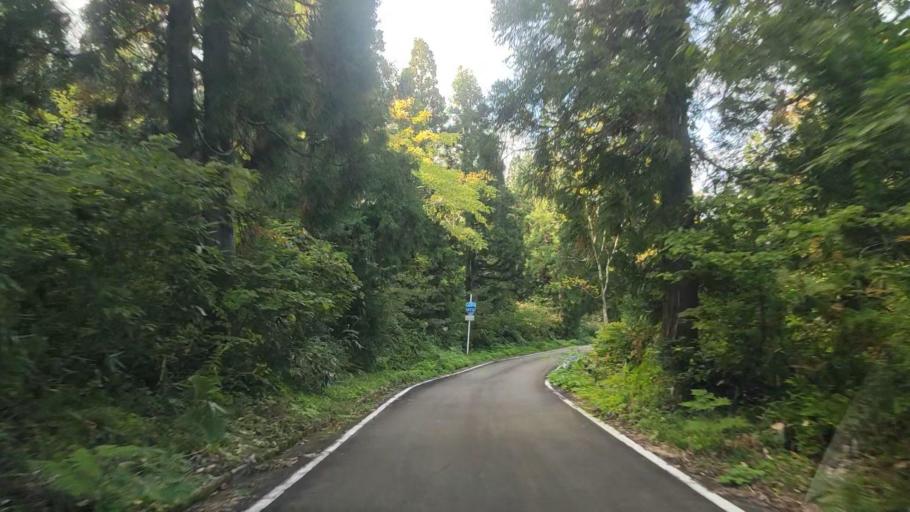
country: JP
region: Toyama
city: Yatsuomachi-higashikumisaka
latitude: 36.3680
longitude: 137.0759
